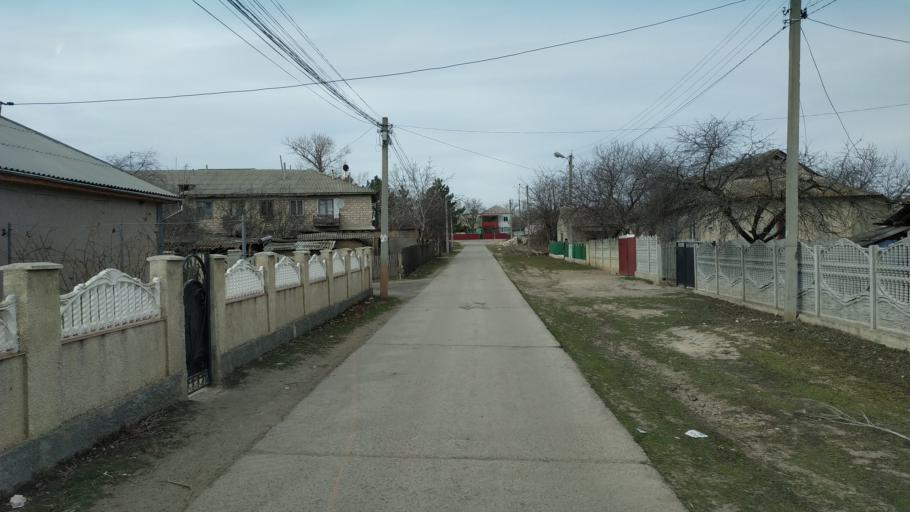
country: MD
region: Hincesti
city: Dancu
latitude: 46.8579
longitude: 28.2510
